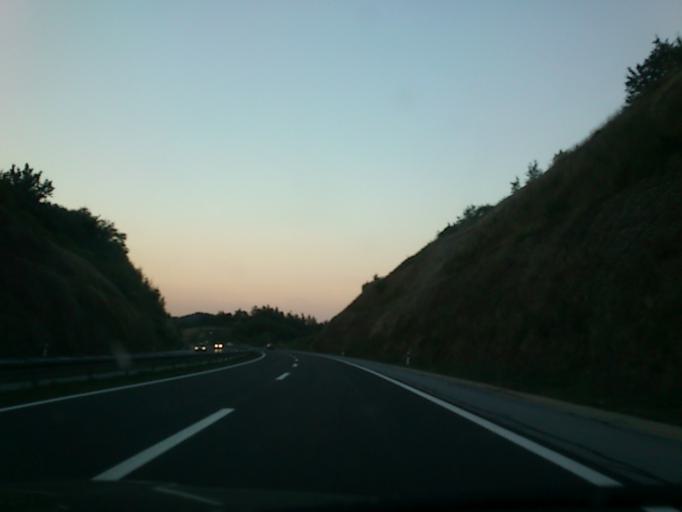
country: HR
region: Karlovacka
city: Ostarije
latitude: 45.1446
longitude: 15.2733
